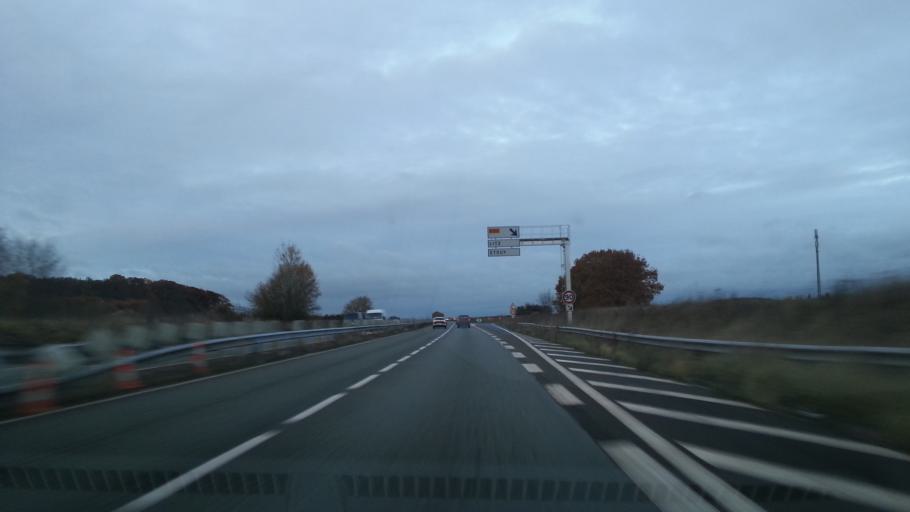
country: FR
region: Picardie
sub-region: Departement de l'Oise
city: Agnetz
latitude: 49.4092
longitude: 2.3446
